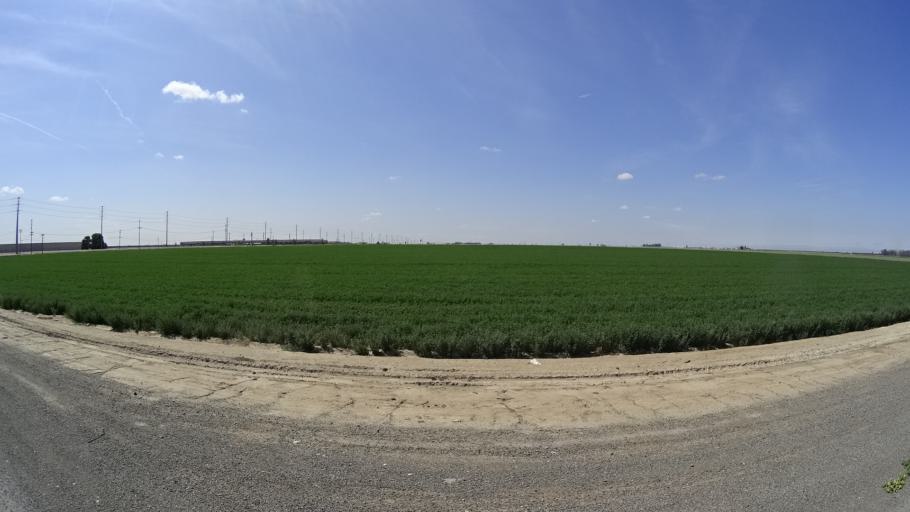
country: US
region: California
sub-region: Kings County
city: Home Garden
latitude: 36.2693
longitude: -119.6572
